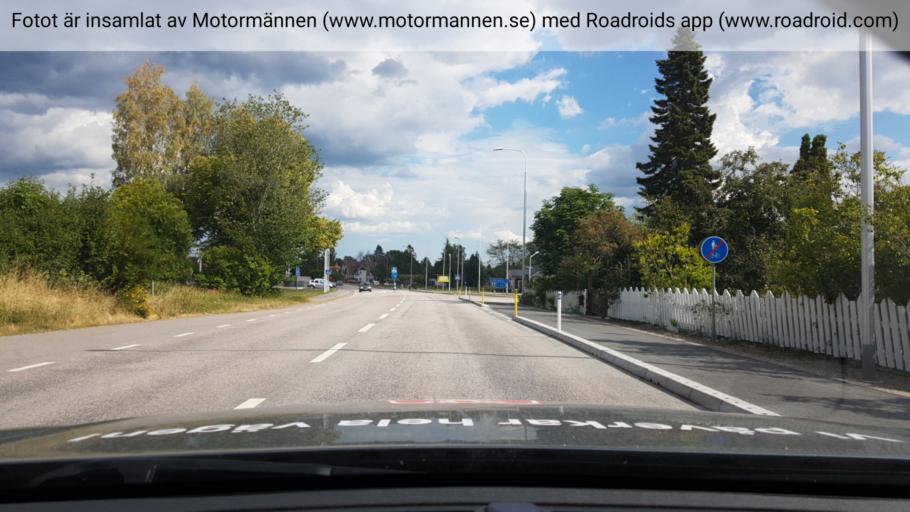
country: SE
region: Uppsala
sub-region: Heby Kommun
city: Morgongava
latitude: 59.9340
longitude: 16.9544
